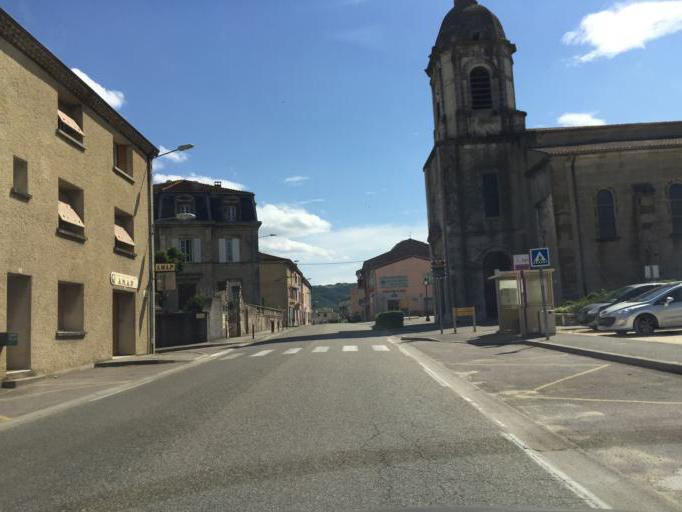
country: FR
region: Rhone-Alpes
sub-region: Departement de l'Ardeche
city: Saint-Jean-de-Muzols
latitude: 45.0836
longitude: 4.8156
